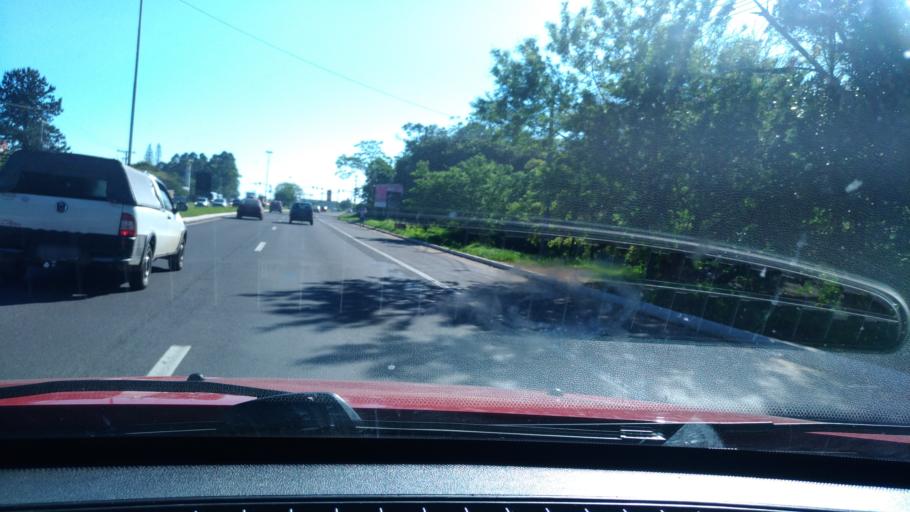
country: BR
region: Rio Grande do Sul
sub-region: Viamao
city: Viamao
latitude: -30.0878
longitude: -51.0590
